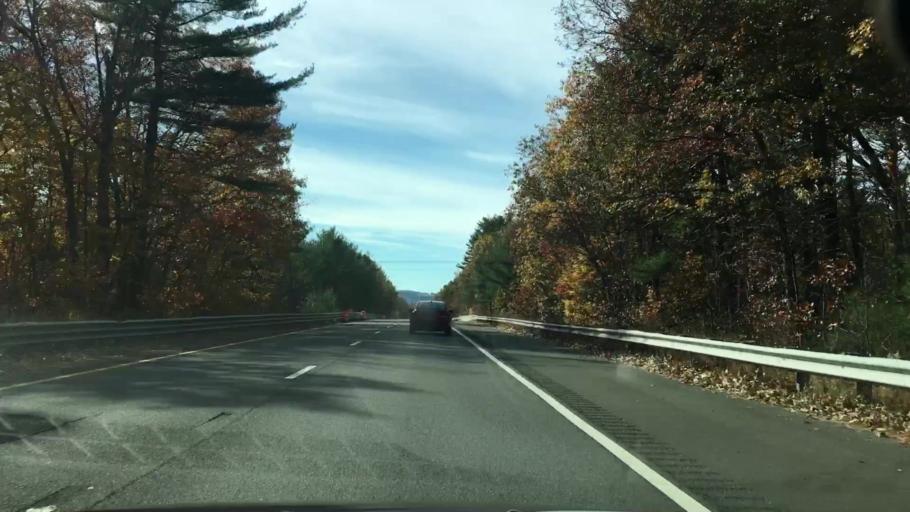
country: US
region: Massachusetts
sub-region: Franklin County
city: Bernardston
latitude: 42.6402
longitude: -72.5720
